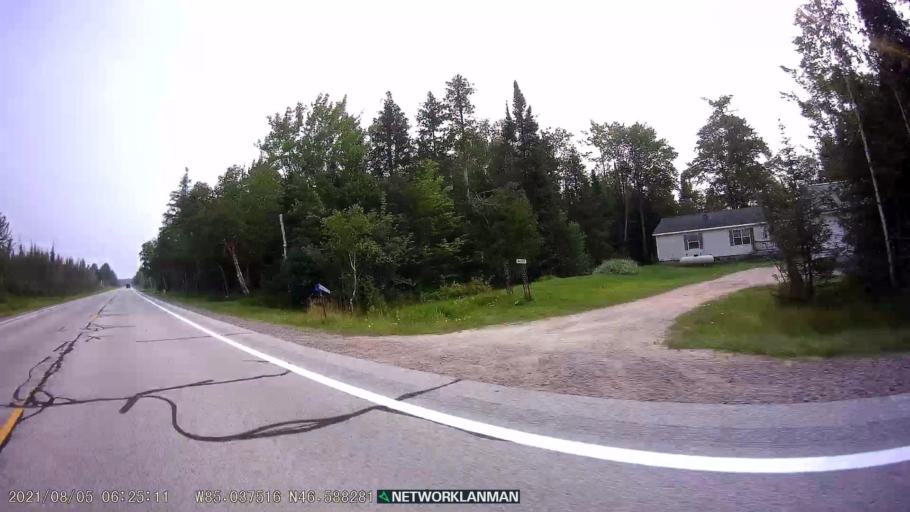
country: US
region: Michigan
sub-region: Luce County
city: Newberry
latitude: 46.5889
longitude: -85.0375
